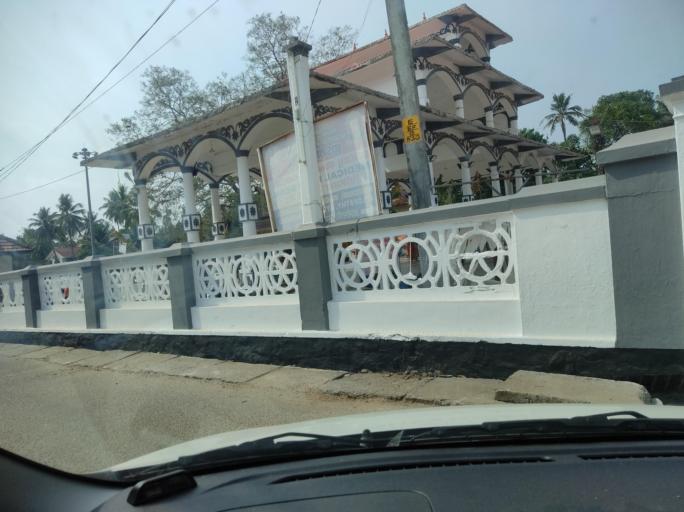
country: IN
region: Kerala
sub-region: Kottayam
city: Kottayam
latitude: 9.6735
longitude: 76.5604
